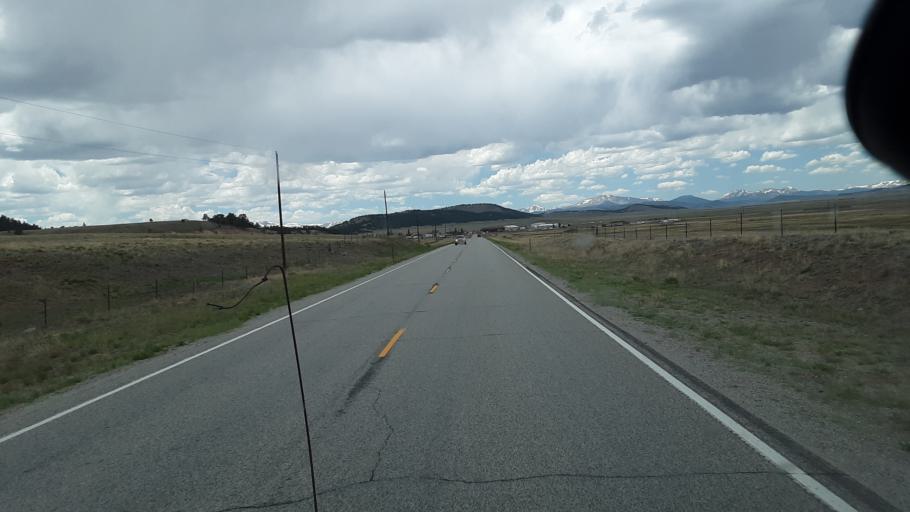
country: US
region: Colorado
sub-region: Park County
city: Fairplay
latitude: 39.0147
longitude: -105.7871
